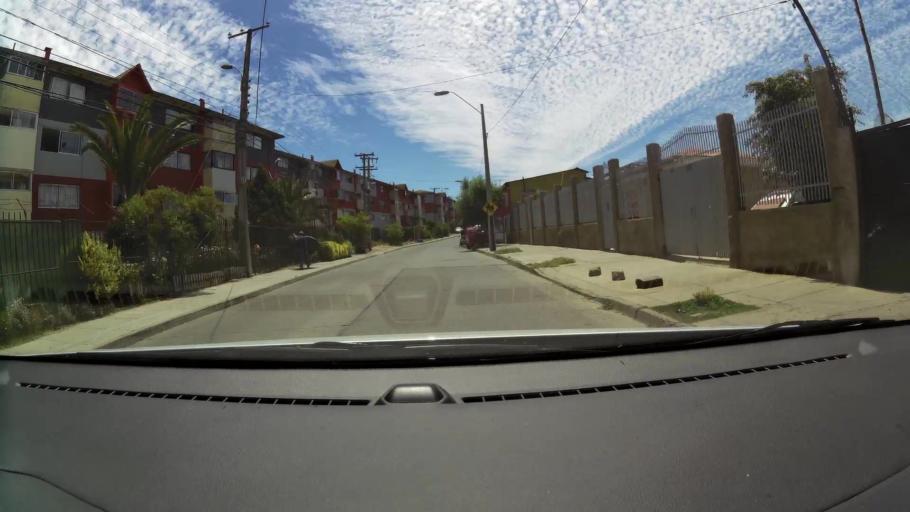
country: CL
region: Valparaiso
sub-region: Provincia de Valparaiso
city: Vina del Mar
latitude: -33.0661
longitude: -71.5683
